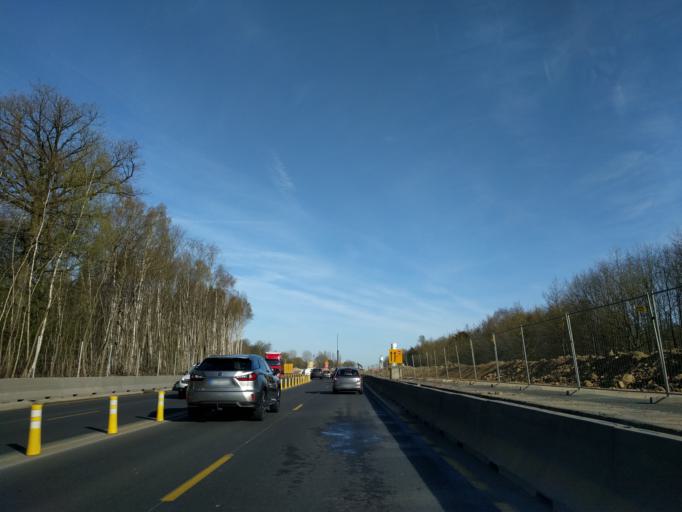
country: FR
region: Ile-de-France
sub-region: Departement du Val-de-Marne
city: Boissy-Saint-Leger
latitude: 48.7395
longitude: 2.5159
